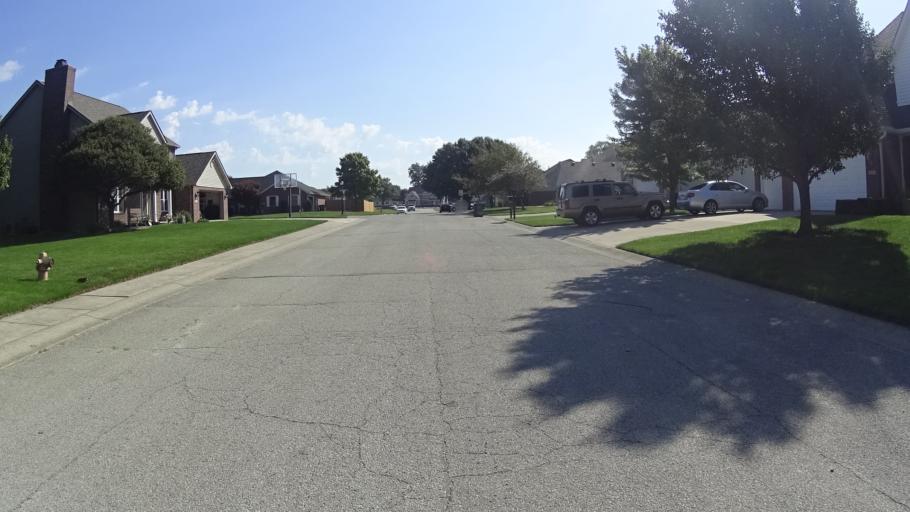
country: US
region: Indiana
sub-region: Madison County
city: Lapel
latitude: 40.0568
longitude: -85.8488
